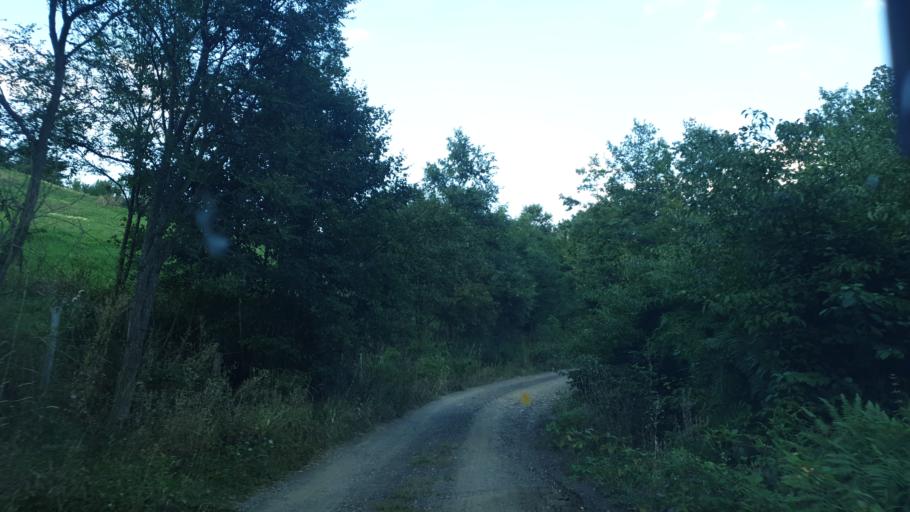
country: RS
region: Central Serbia
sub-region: Zlatiborski Okrug
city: Kosjeric
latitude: 44.0118
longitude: 19.9939
